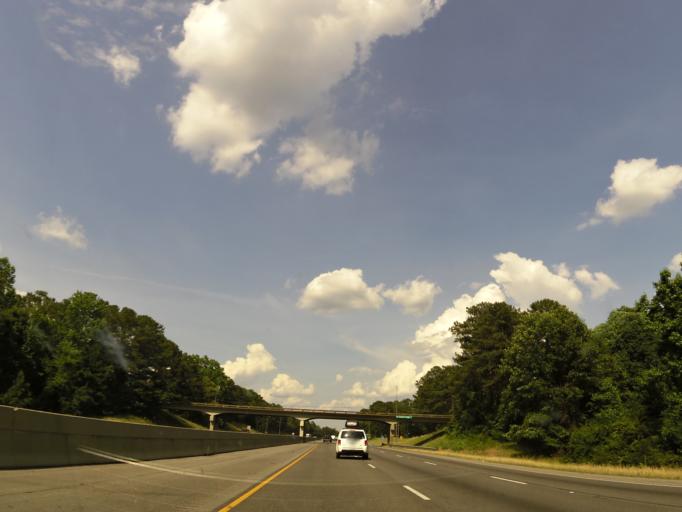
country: US
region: Alabama
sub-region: Tuscaloosa County
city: Coaling
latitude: 33.1877
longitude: -87.3299
